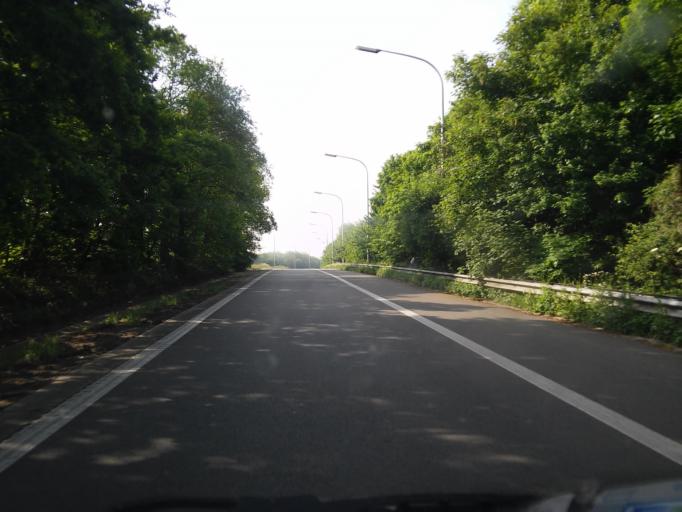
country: BE
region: Flanders
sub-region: Provincie Antwerpen
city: Rumst
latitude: 51.0823
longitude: 4.4430
